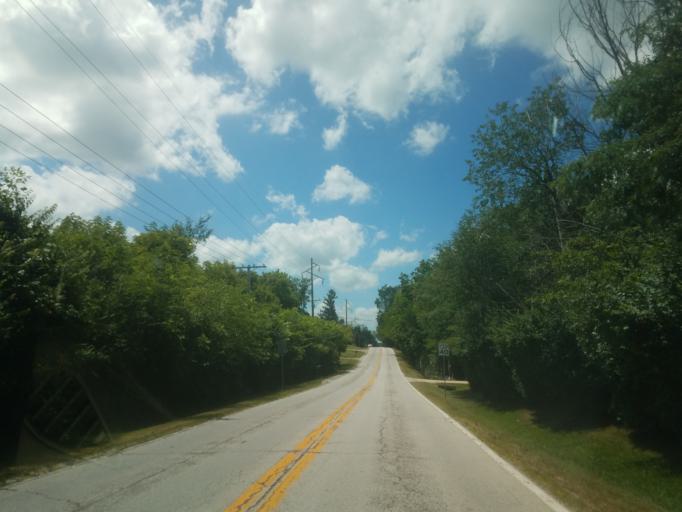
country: US
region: Illinois
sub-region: McLean County
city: Bloomington
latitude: 40.4589
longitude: -89.0122
